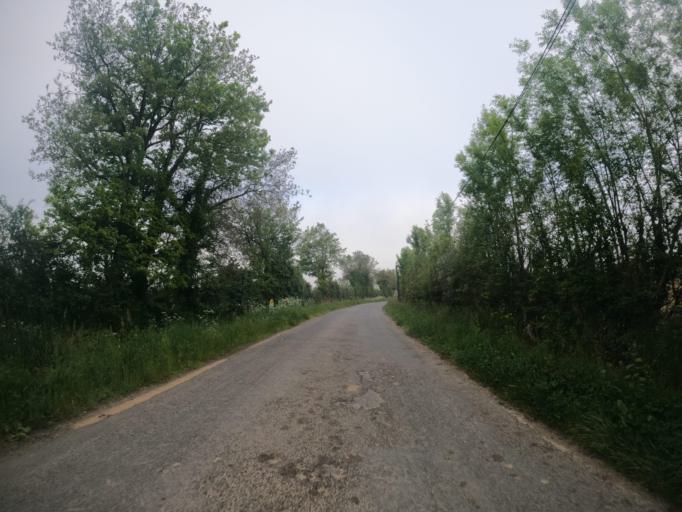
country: FR
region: Poitou-Charentes
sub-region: Departement des Deux-Sevres
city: Chiche
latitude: 46.8893
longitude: -0.3381
